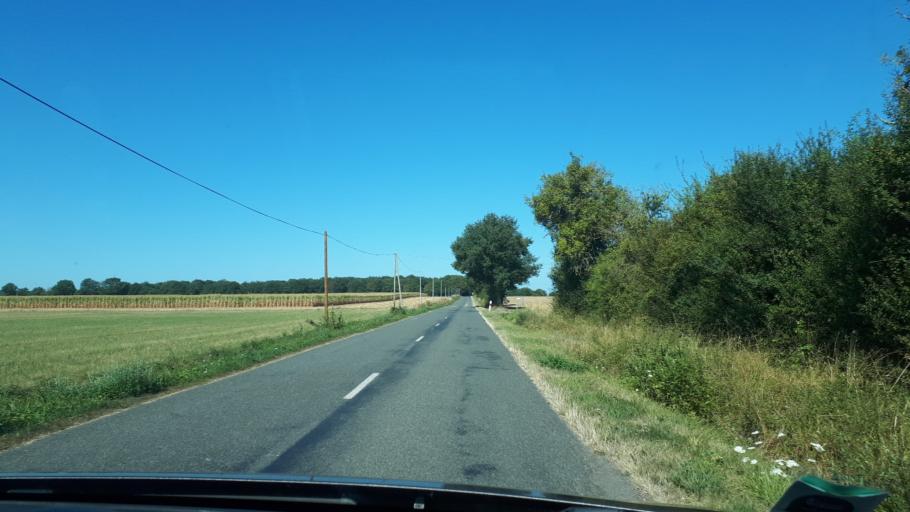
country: FR
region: Centre
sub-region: Departement du Loiret
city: Briare
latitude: 47.5922
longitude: 2.7163
